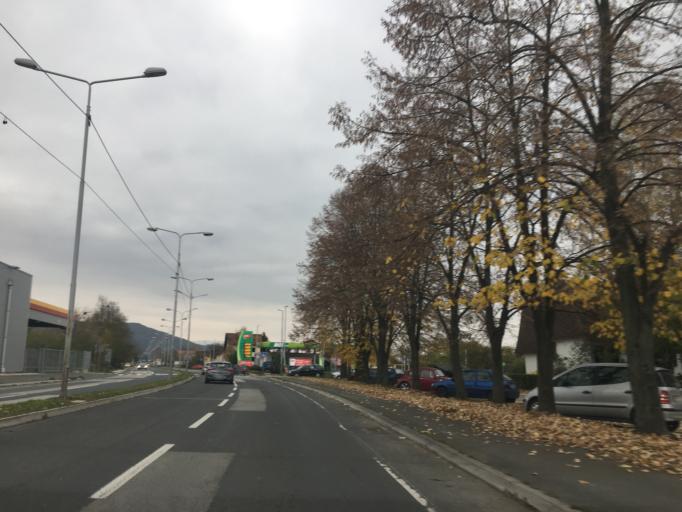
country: RS
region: Central Serbia
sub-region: Raski Okrug
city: Kraljevo
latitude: 43.7257
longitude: 20.7180
